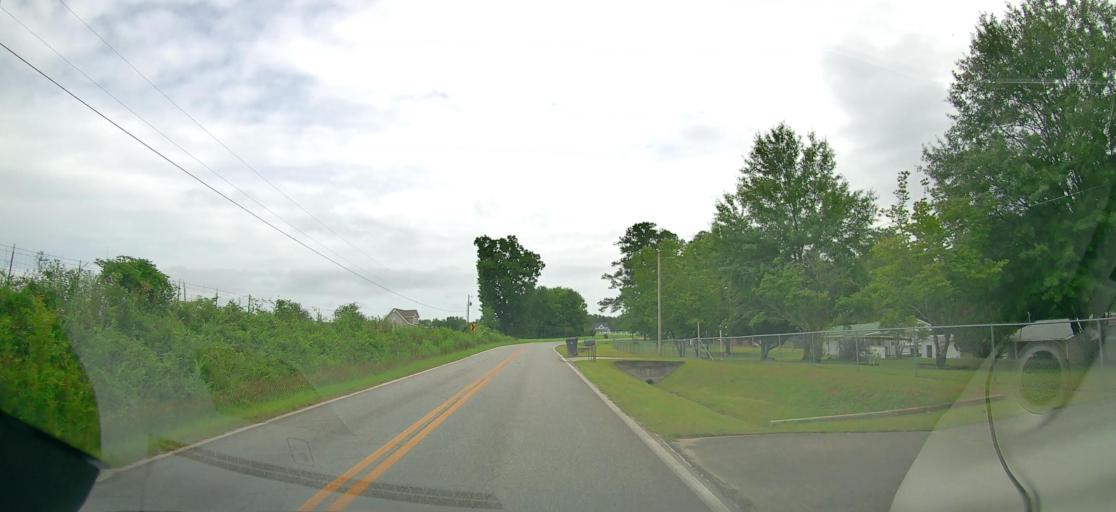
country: US
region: Georgia
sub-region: Bibb County
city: West Point
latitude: 32.7599
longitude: -83.7936
